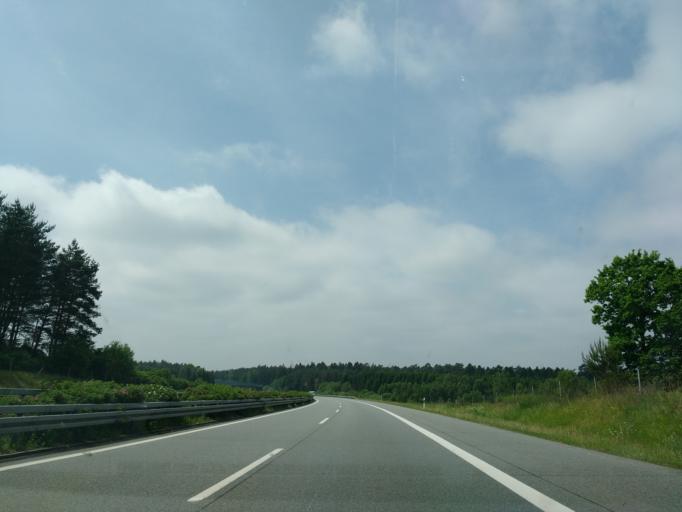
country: DE
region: Schleswig-Holstein
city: Gross Gronau
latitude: 53.8153
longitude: 10.7882
